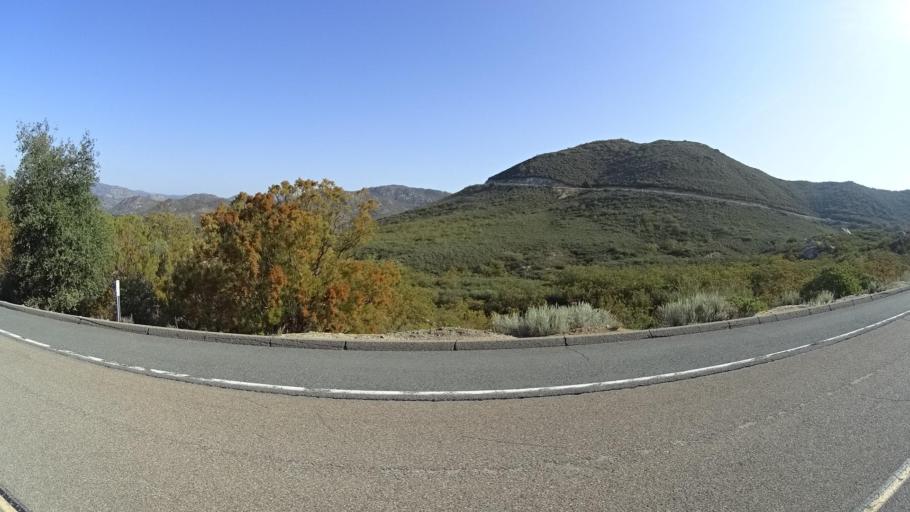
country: US
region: California
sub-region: San Diego County
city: Pine Valley
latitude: 32.8148
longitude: -116.5136
